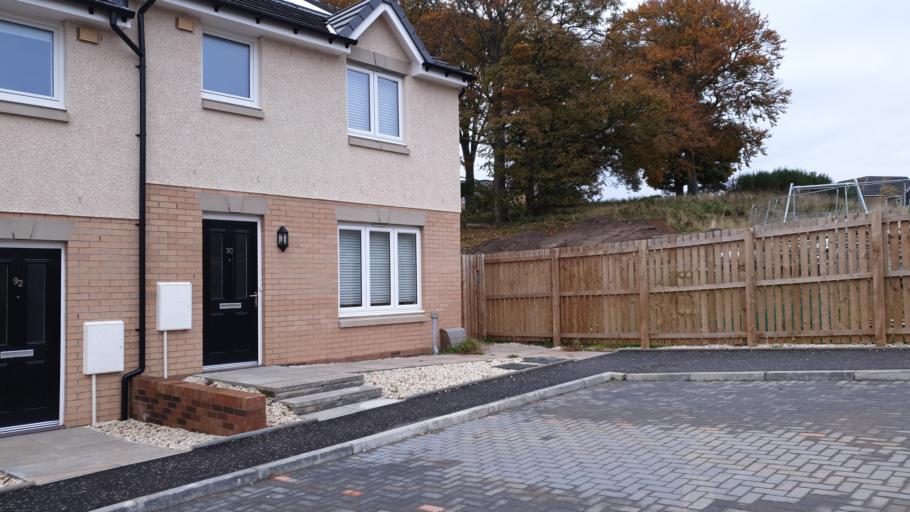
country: GB
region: Scotland
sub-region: South Lanarkshire
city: Uddingston
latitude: 55.8261
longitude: -4.1263
